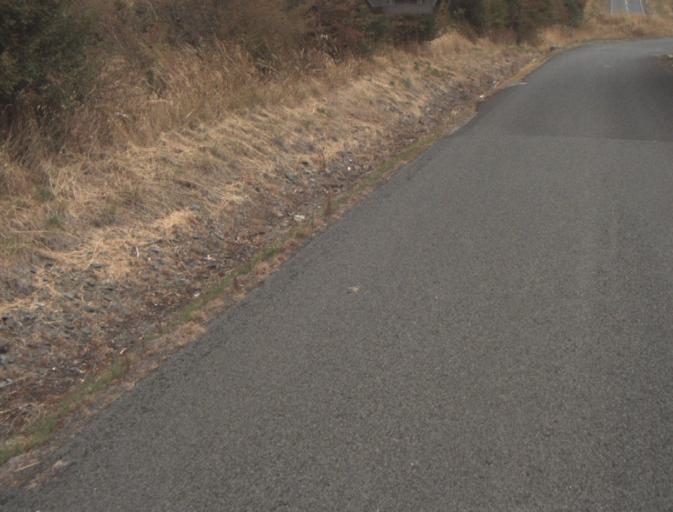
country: AU
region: Tasmania
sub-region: Northern Midlands
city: Evandale
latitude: -41.5047
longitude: 147.2524
